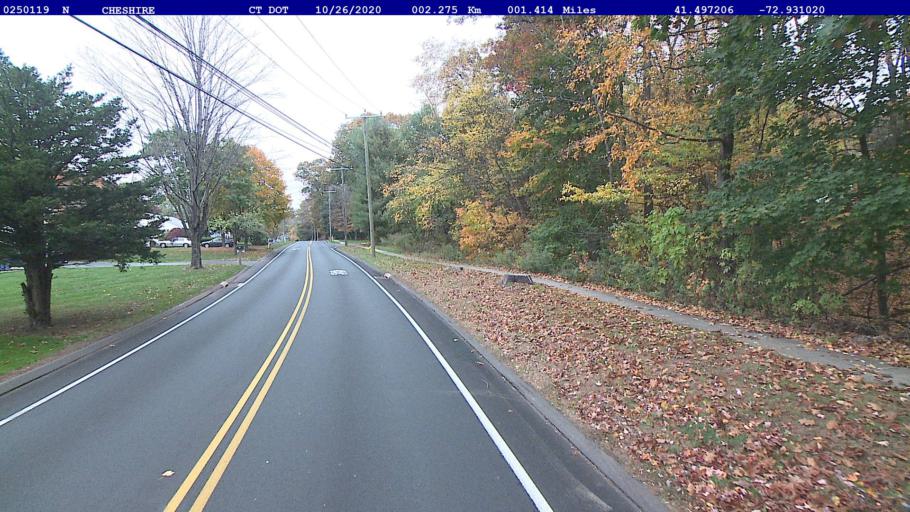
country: US
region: Connecticut
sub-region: New Haven County
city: Cheshire
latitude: 41.4972
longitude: -72.9310
